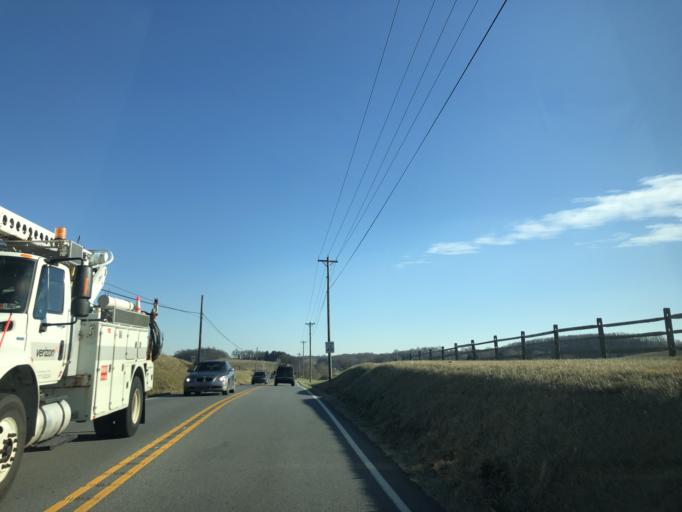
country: US
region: Pennsylvania
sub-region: Chester County
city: Upland
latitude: 39.9113
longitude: -75.8087
